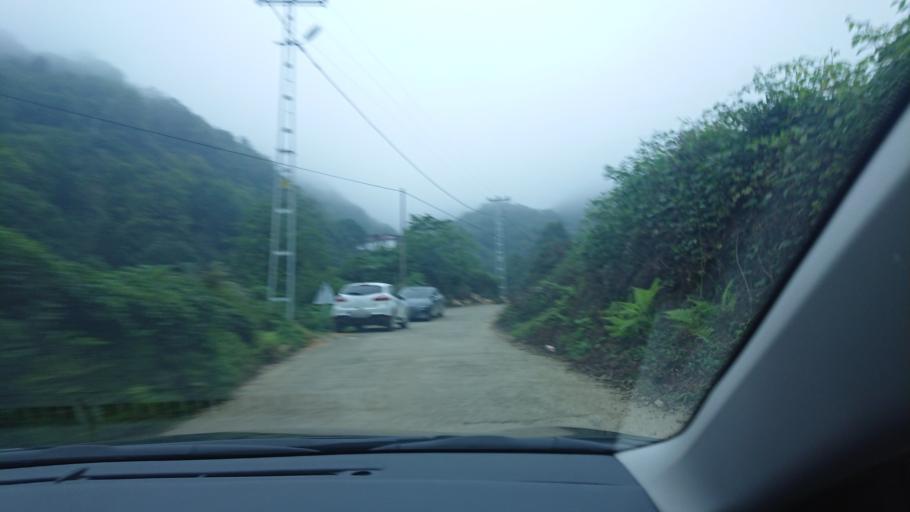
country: TR
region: Rize
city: Kaptanpasa
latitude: 41.0451
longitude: 40.8050
